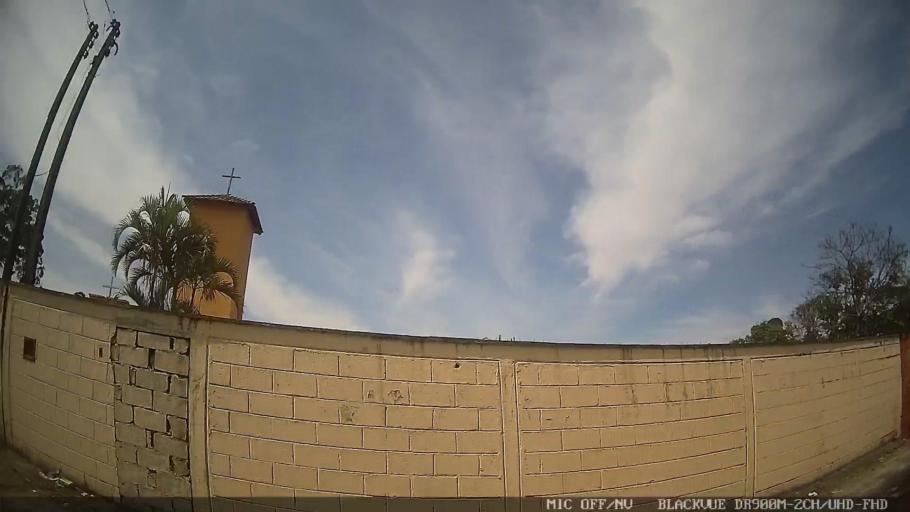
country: BR
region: Sao Paulo
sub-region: Suzano
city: Suzano
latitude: -23.4908
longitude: -46.2659
